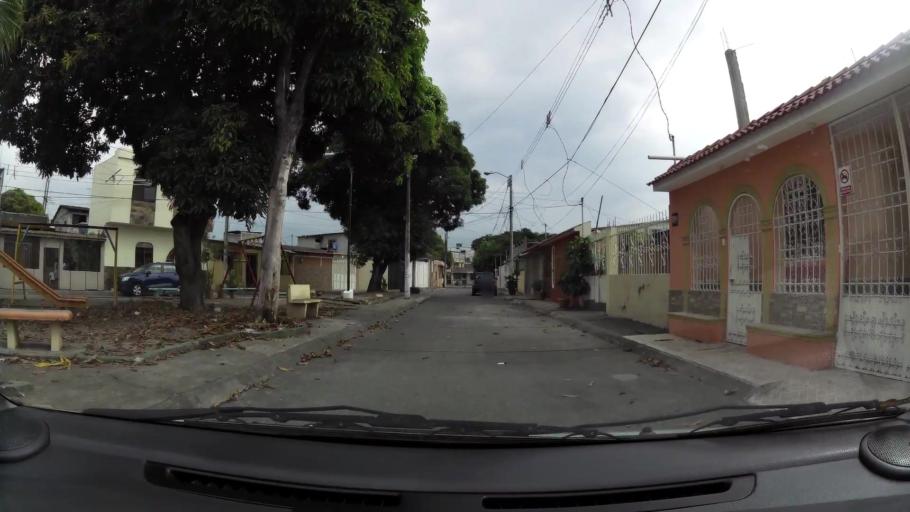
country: EC
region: Guayas
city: Eloy Alfaro
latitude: -2.1185
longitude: -79.8859
